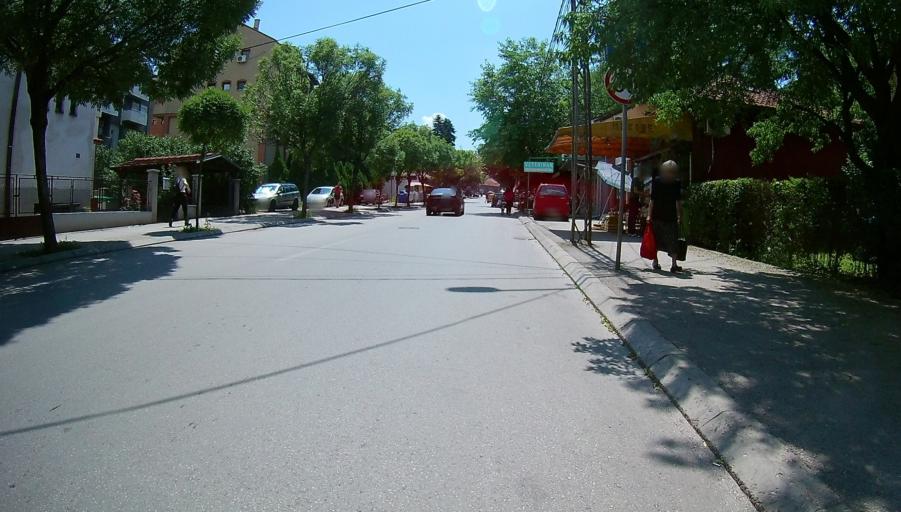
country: RS
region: Central Serbia
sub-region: Nisavski Okrug
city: Nis
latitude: 43.3109
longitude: 21.8933
